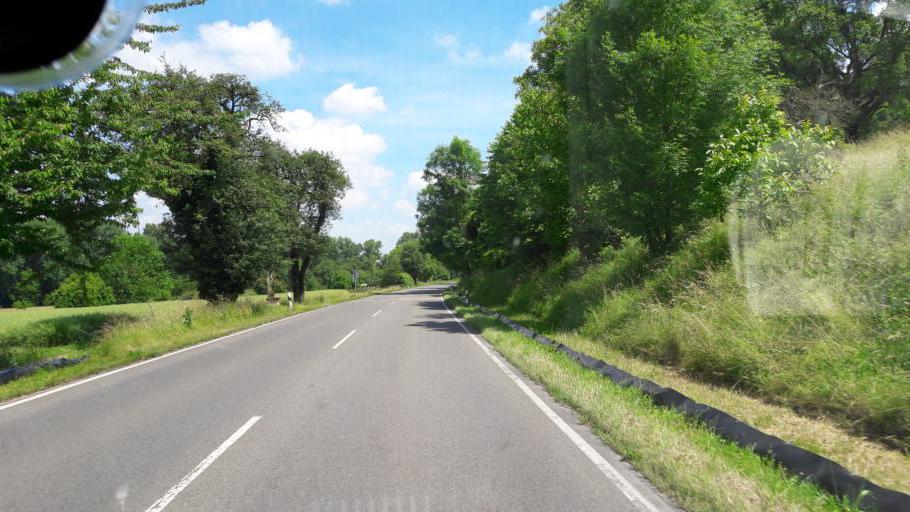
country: DE
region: Baden-Wuerttemberg
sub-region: Karlsruhe Region
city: Weingarten
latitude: 49.0745
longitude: 8.5439
